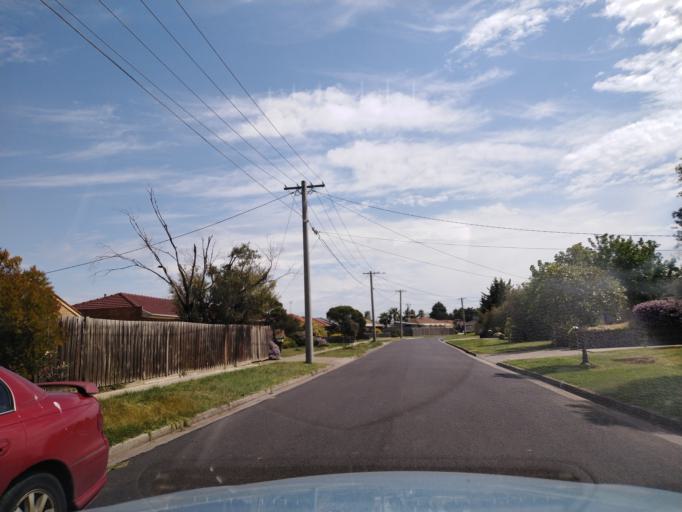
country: AU
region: Victoria
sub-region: Wyndham
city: Hoppers Crossing
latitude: -37.8612
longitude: 144.7095
